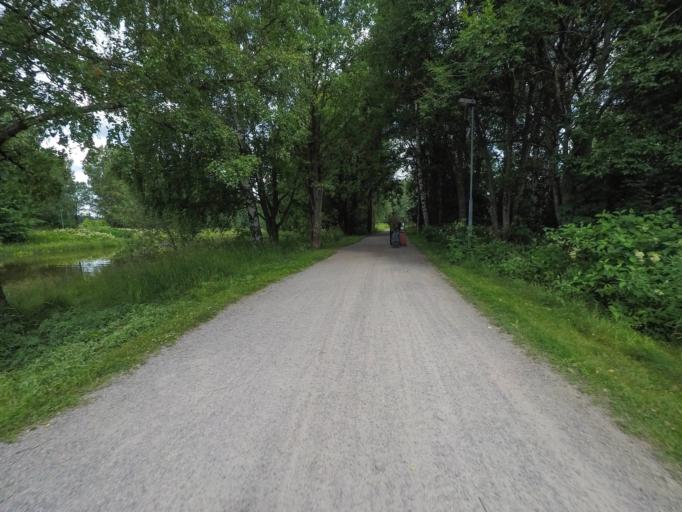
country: FI
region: Uusimaa
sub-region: Helsinki
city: Vantaa
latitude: 60.2320
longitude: 24.9906
